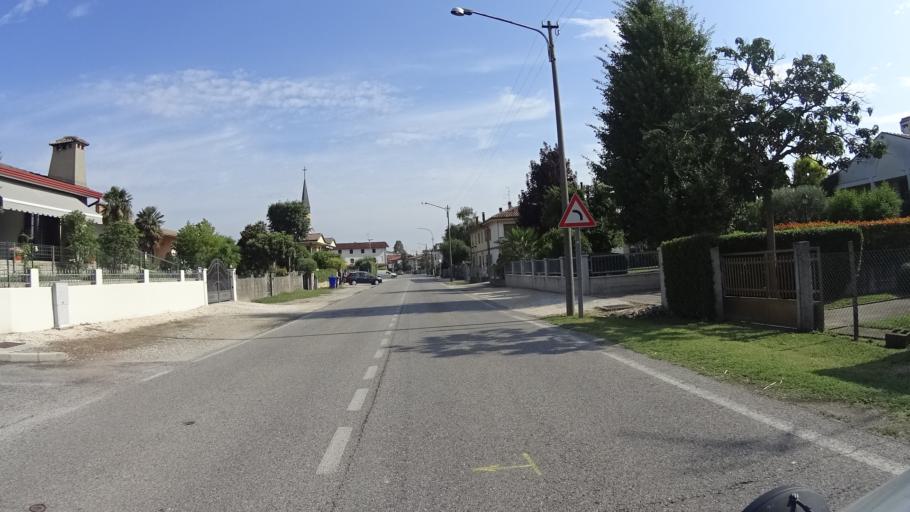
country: IT
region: Veneto
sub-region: Provincia di Venezia
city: Lugugnana
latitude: 45.7289
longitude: 12.9578
